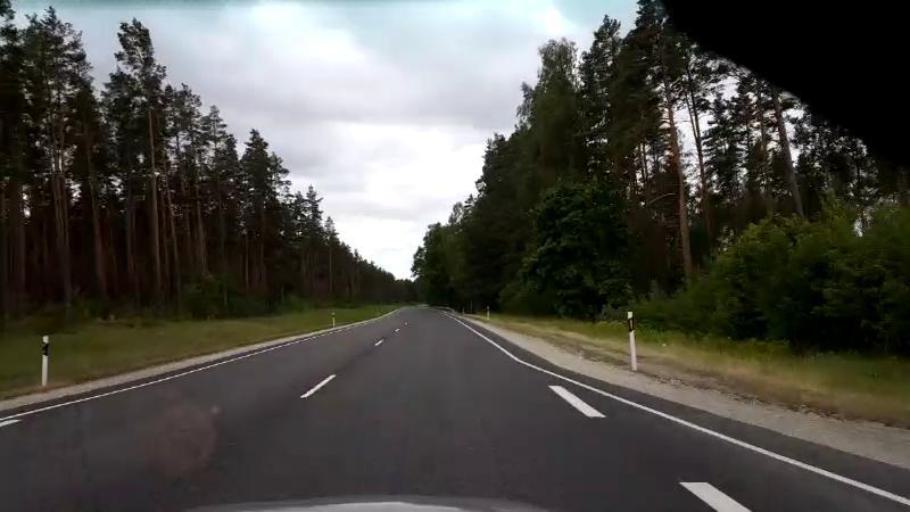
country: EE
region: Paernumaa
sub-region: Paernu linn
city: Parnu
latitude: 58.2646
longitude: 24.5497
